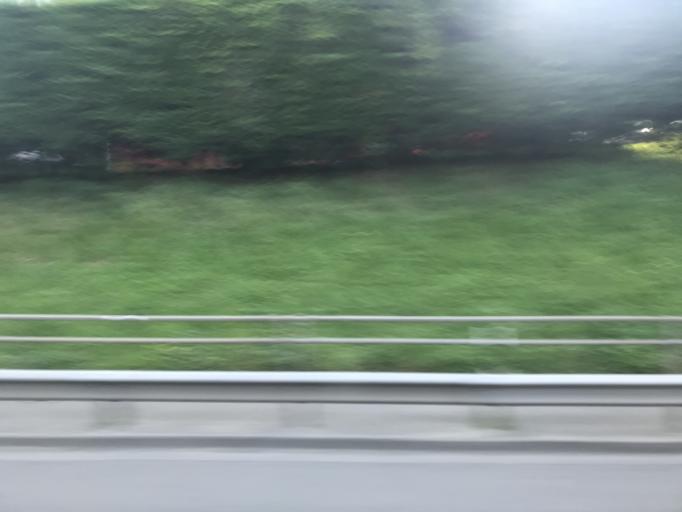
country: ES
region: Basque Country
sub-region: Provincia de Guipuzcoa
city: Andoain
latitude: 43.2232
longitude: -2.0255
